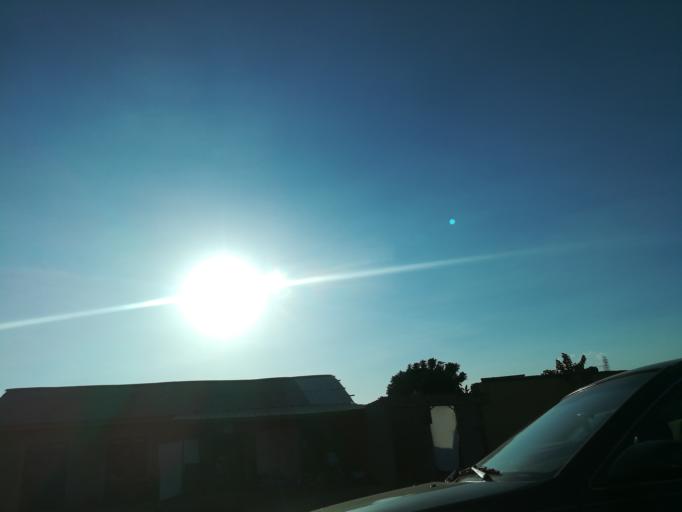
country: NG
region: Lagos
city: Ikorodu
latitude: 6.5911
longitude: 3.5178
